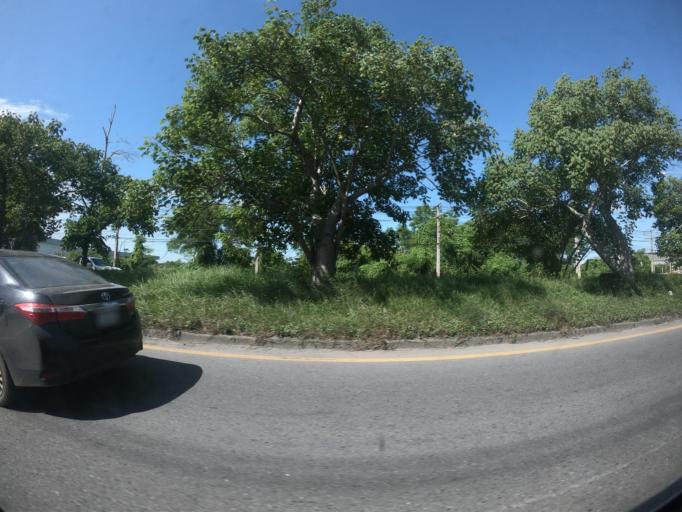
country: TH
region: Nakhon Nayok
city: Nakhon Nayok
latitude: 14.2299
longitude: 101.1688
